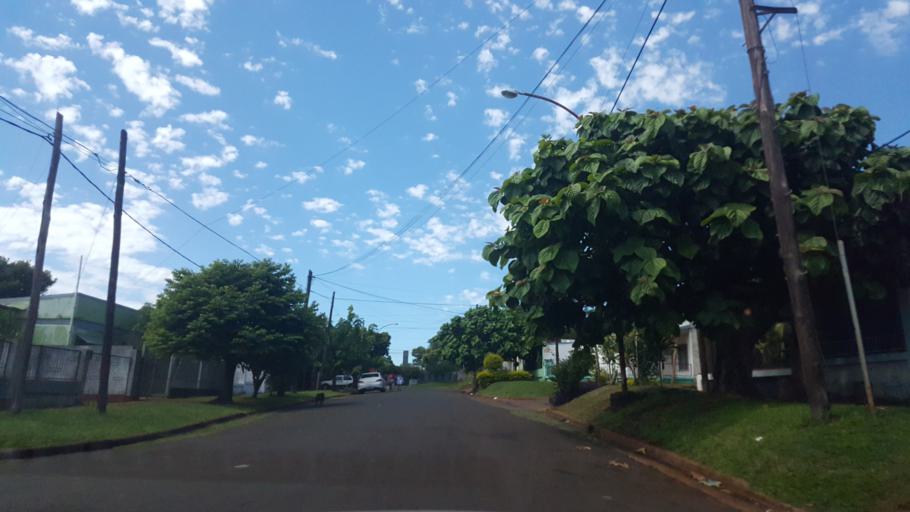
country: AR
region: Misiones
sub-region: Departamento de Capital
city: Posadas
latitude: -27.3874
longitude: -55.9168
